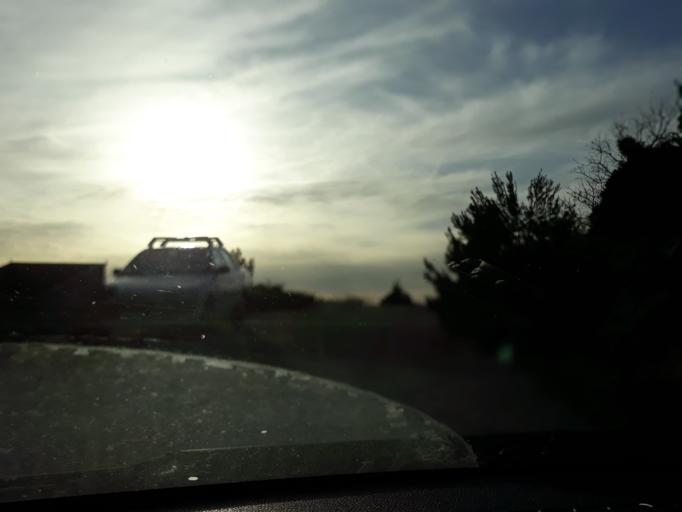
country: GR
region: Attica
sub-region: Nomarchia Anatolikis Attikis
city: Afidnes
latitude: 38.2152
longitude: 23.8116
